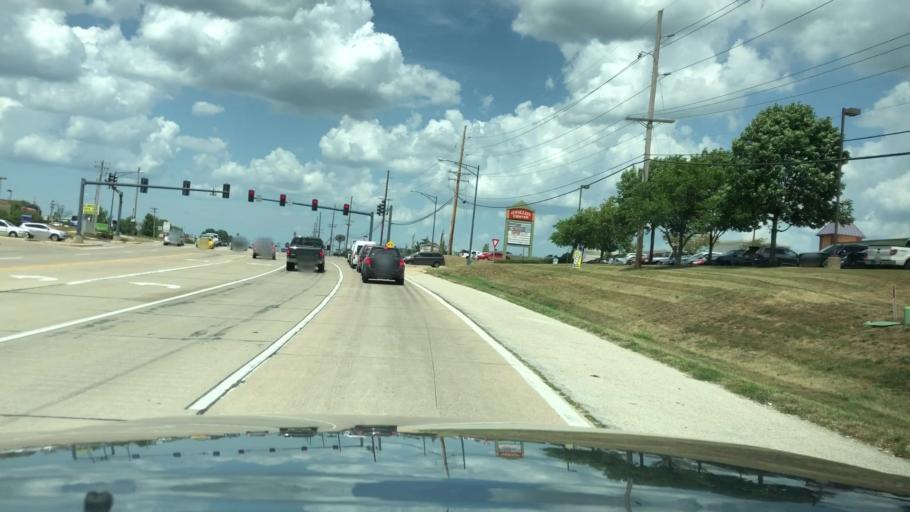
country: US
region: Missouri
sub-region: Saint Charles County
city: O'Fallon
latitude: 38.7935
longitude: -90.6986
